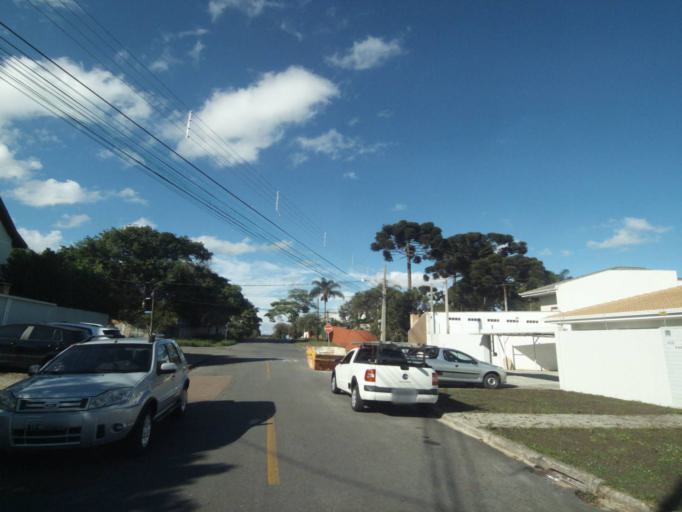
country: BR
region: Parana
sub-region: Curitiba
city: Curitiba
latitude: -25.3915
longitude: -49.2542
